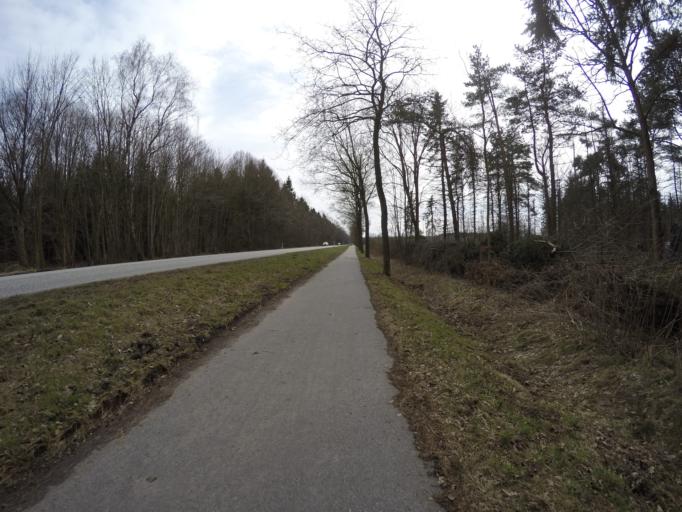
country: DE
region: Schleswig-Holstein
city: Heidmoor
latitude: 53.8210
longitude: 9.8817
